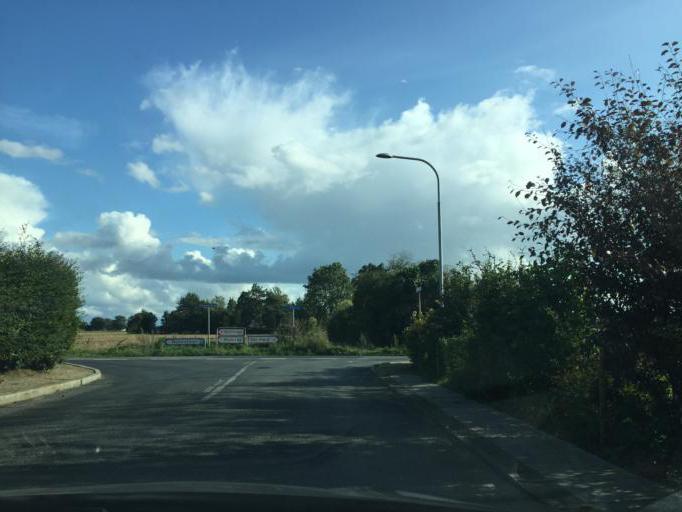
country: DK
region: South Denmark
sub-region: Kerteminde Kommune
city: Langeskov
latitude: 55.3147
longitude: 10.5323
